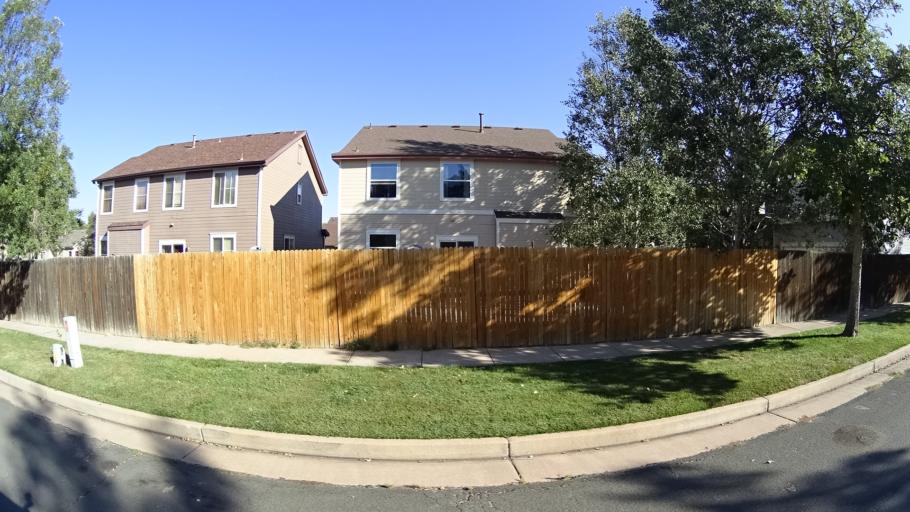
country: US
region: Colorado
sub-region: El Paso County
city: Cimarron Hills
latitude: 38.8759
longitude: -104.6999
